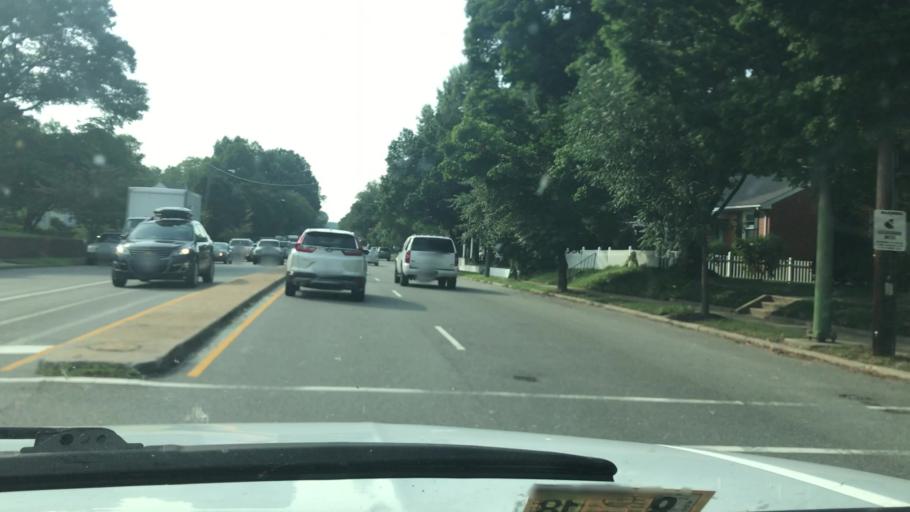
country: US
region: Virginia
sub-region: Henrico County
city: Dumbarton
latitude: 37.5696
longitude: -77.4963
